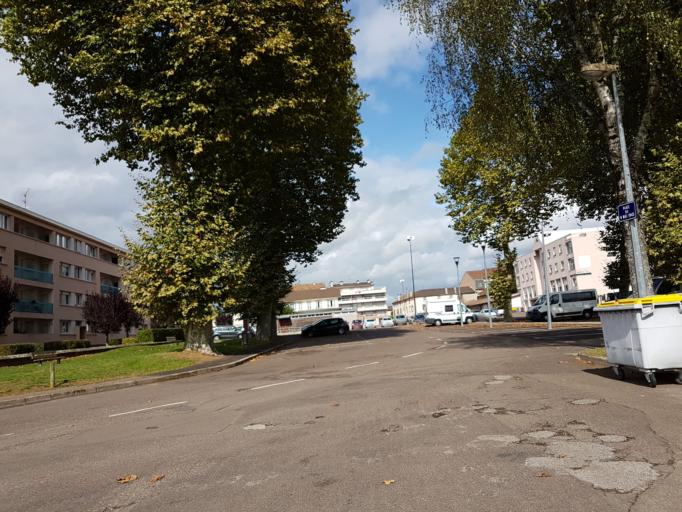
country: FR
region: Franche-Comte
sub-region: Departement de la Haute-Saone
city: Saint-Sauveur
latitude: 47.8116
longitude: 6.3805
